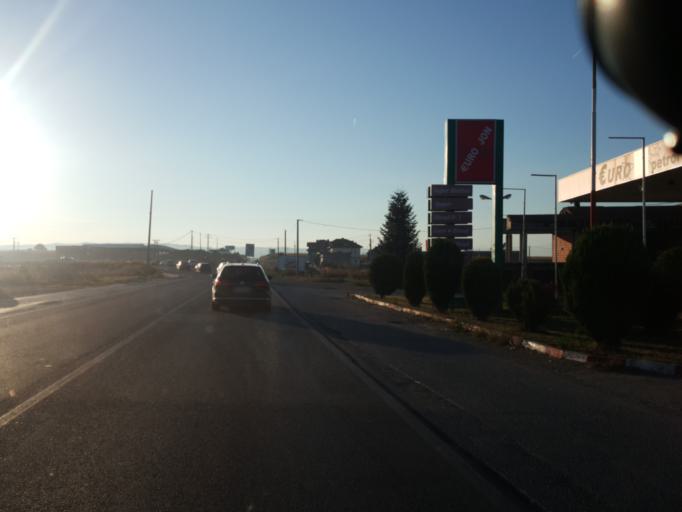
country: XK
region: Prizren
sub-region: Komuna e Malisheves
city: Llazice
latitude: 42.5763
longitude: 20.7068
